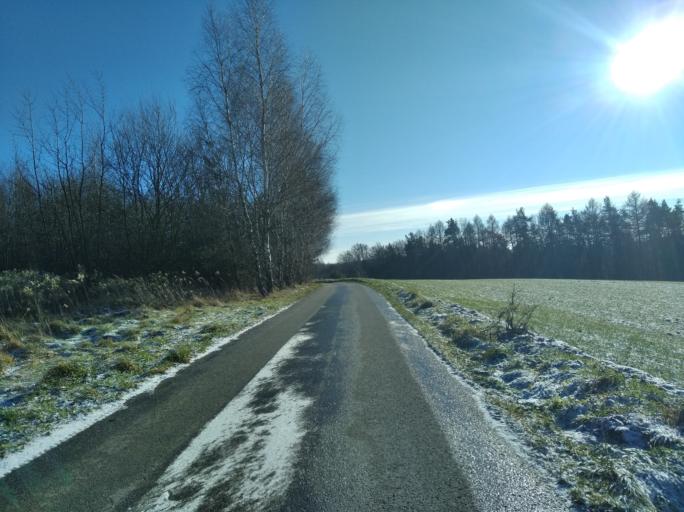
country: PL
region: Subcarpathian Voivodeship
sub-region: Powiat ropczycko-sedziszowski
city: Iwierzyce
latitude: 49.9607
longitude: 21.7516
